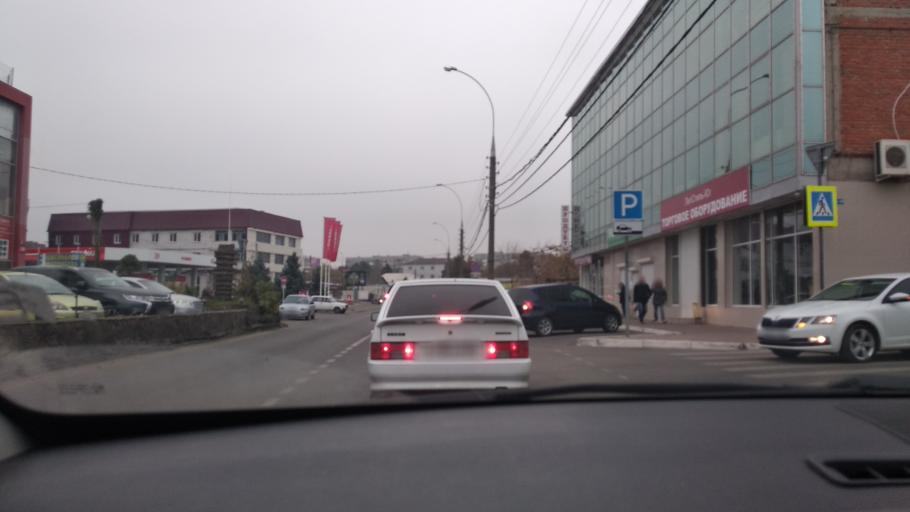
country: RU
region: Krasnodarskiy
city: Krasnodar
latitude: 45.0243
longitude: 39.0086
